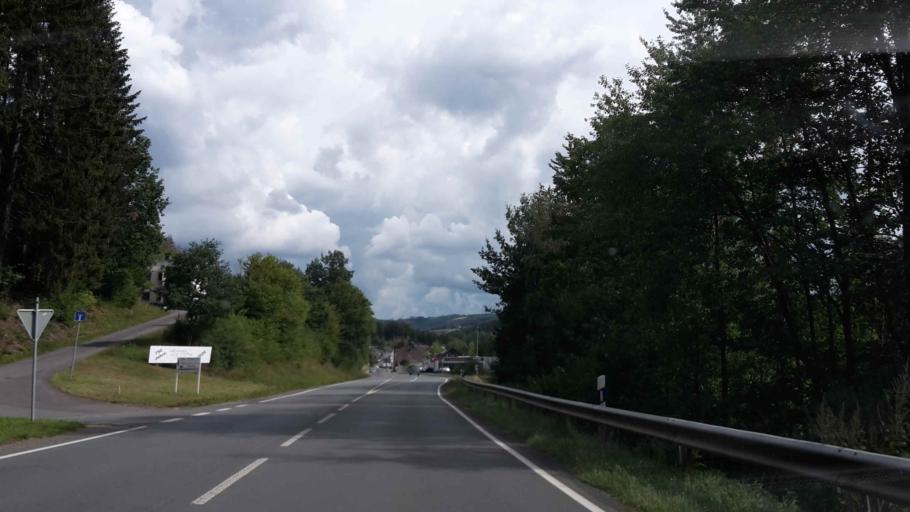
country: DE
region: North Rhine-Westphalia
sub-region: Regierungsbezirk Arnsberg
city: Kirchhundem
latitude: 51.0897
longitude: 8.1131
